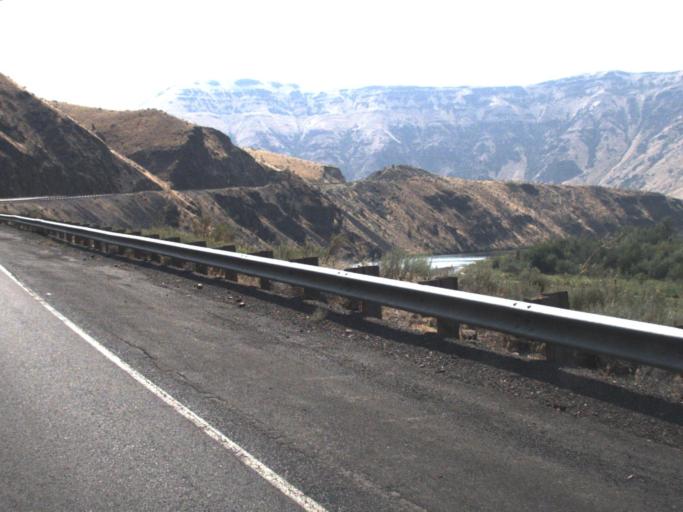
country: US
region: Washington
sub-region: Yakima County
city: Selah
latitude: 46.7606
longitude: -120.4529
